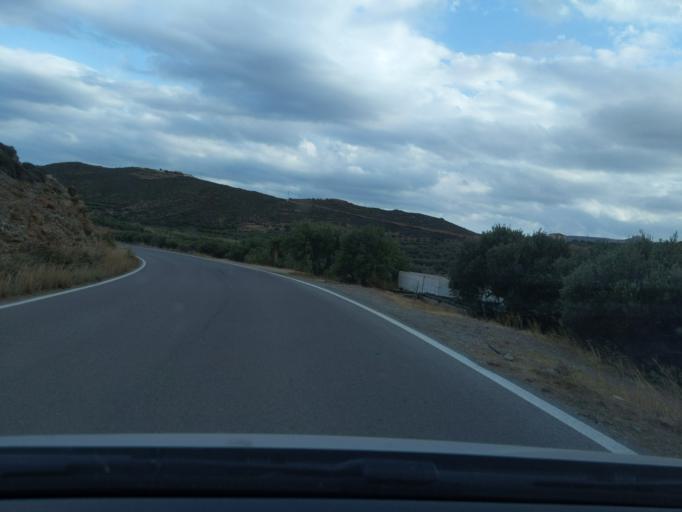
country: GR
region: Crete
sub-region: Nomos Lasithiou
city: Palekastro
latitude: 35.2246
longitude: 26.2570
